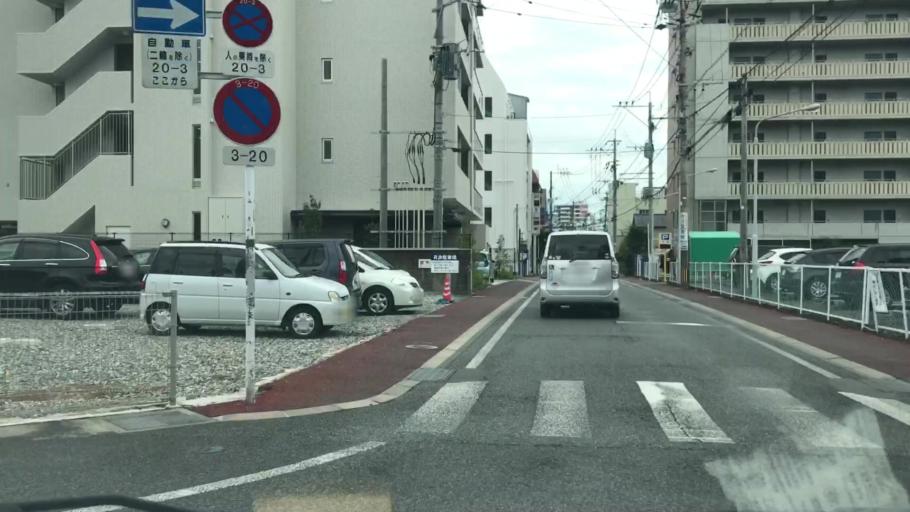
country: JP
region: Saga Prefecture
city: Saga-shi
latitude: 33.2606
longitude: 130.3009
